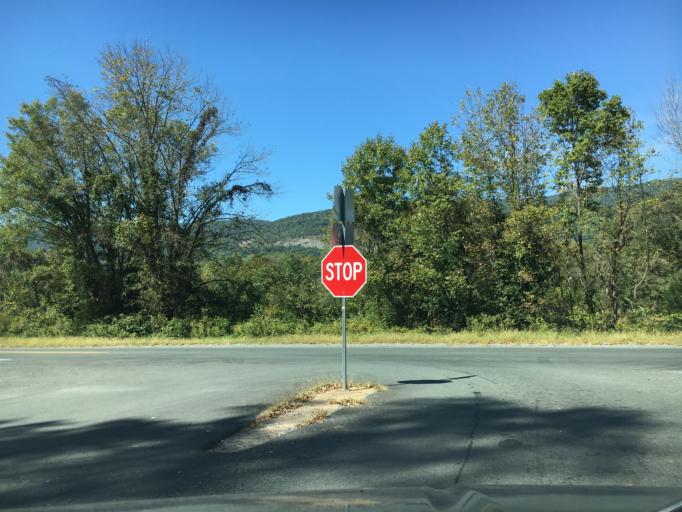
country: US
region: Virginia
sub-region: Albemarle County
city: Crozet
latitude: 38.0277
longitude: -78.7942
